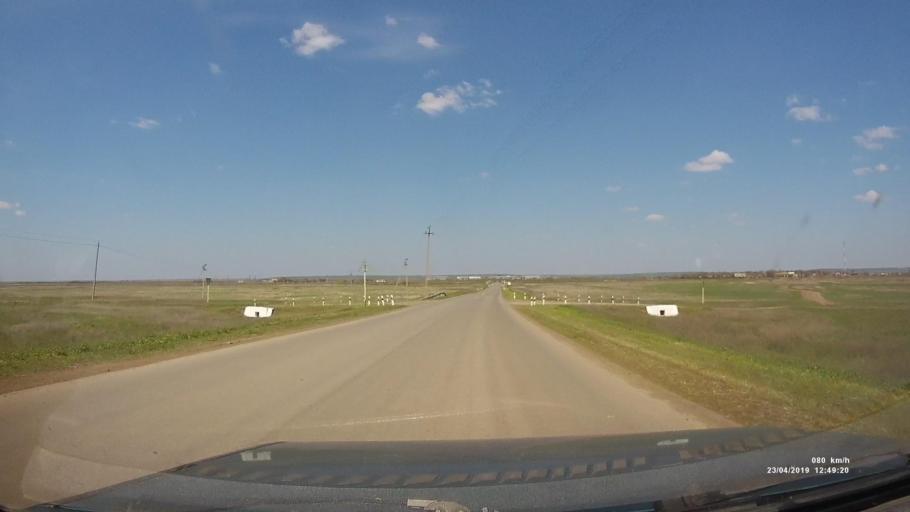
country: RU
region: Kalmykiya
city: Yashalta
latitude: 46.5360
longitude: 42.6390
